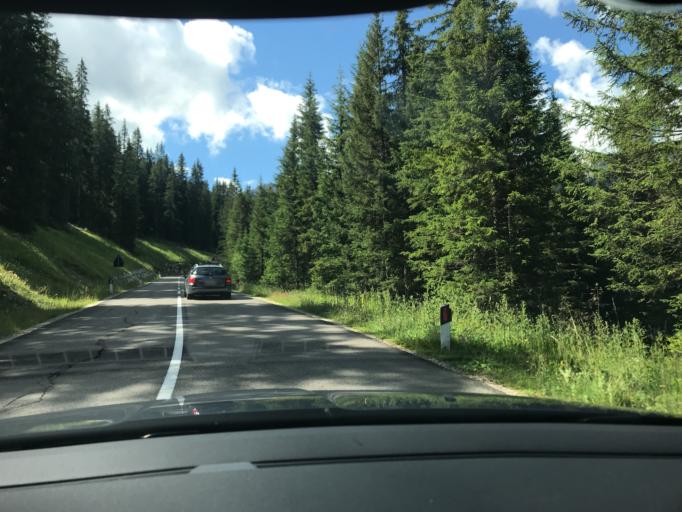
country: IT
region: Veneto
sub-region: Provincia di Belluno
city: Livinallongo del Col di Lana
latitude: 46.5507
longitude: 11.9676
